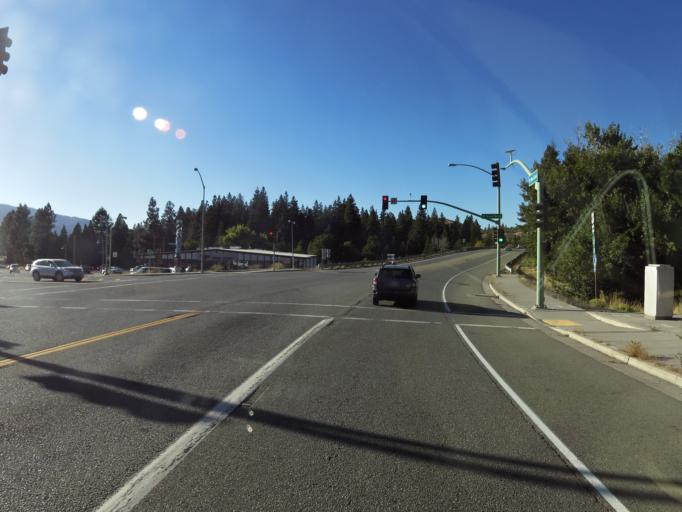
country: US
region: California
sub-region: Siskiyou County
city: Weed
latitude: 41.4227
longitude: -122.3870
